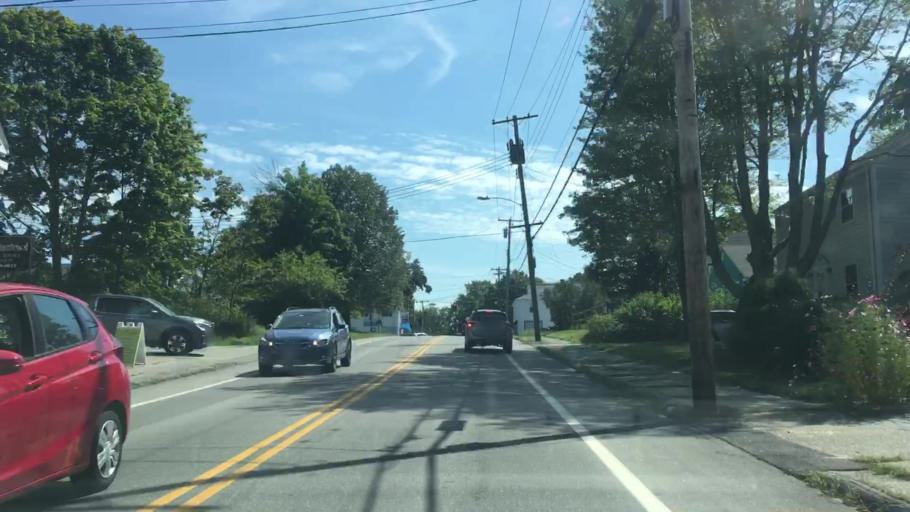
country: US
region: Maine
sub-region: Cumberland County
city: South Portland
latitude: 43.6260
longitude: -70.2503
